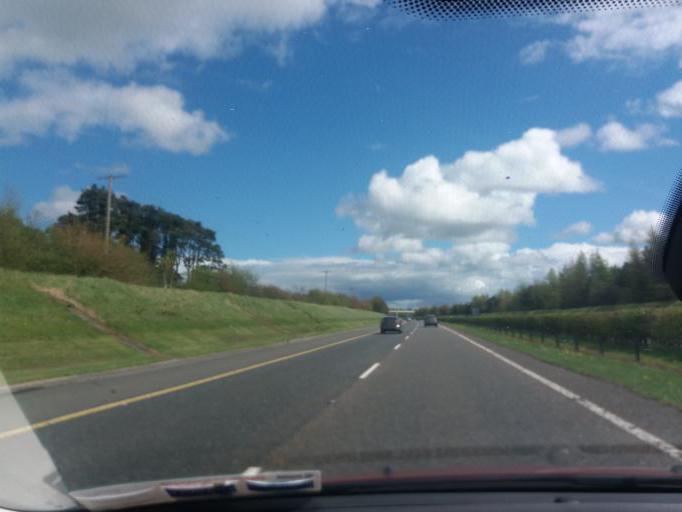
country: IE
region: Leinster
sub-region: Kildare
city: Kildare
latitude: 53.1514
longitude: -6.9005
